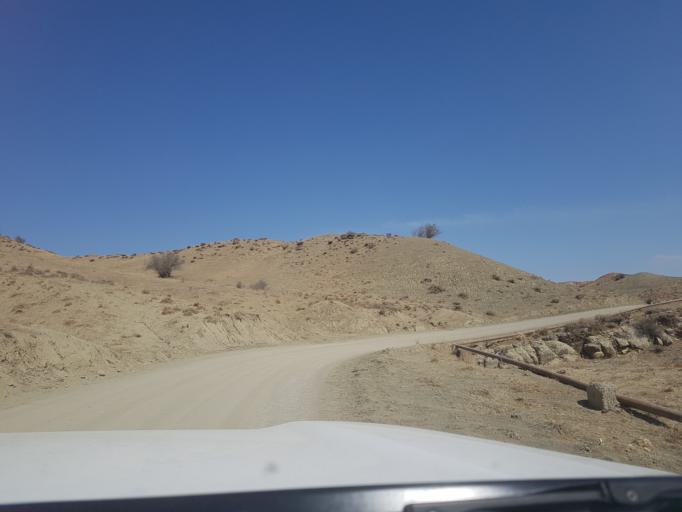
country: TM
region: Ahal
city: Baharly
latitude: 38.2426
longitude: 56.8895
